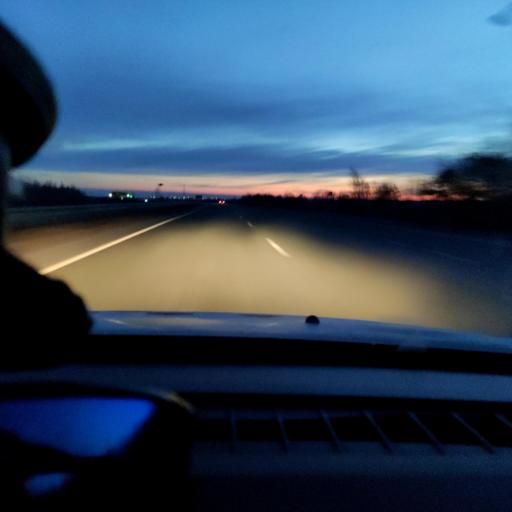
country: RU
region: Samara
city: Novokuybyshevsk
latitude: 53.0031
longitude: 49.9649
